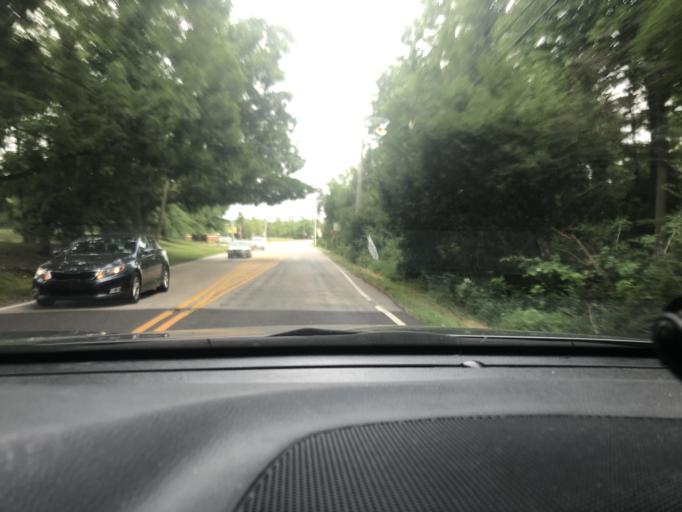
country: US
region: Pennsylvania
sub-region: Montgomery County
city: Spring House
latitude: 40.1951
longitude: -75.2445
